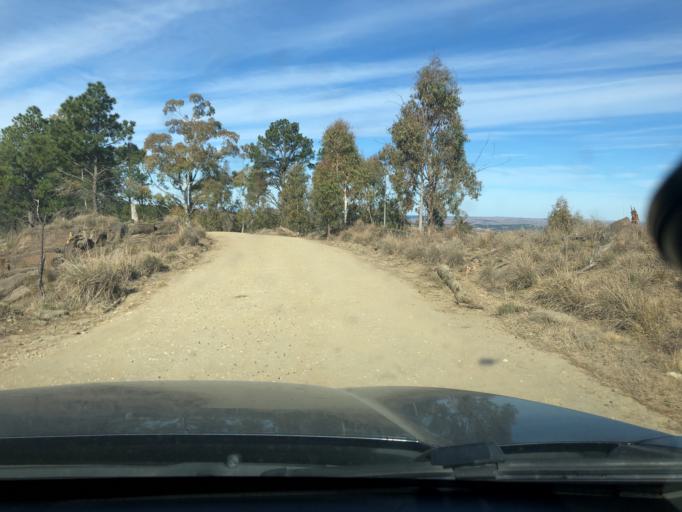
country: AR
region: Cordoba
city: Villa Berna
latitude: -31.9637
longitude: -64.8075
